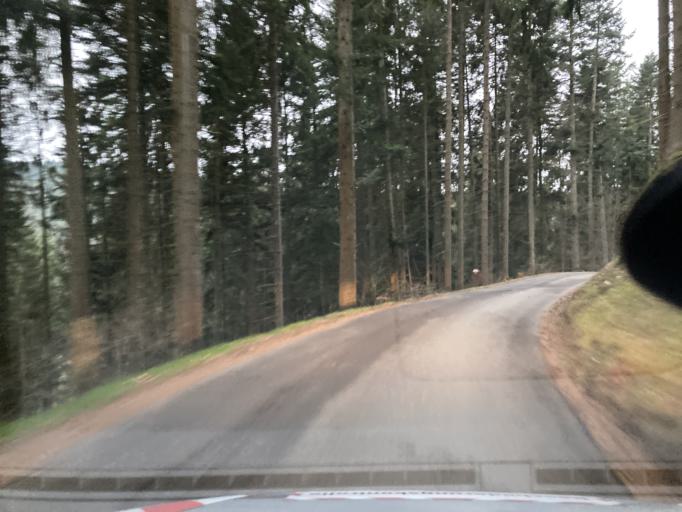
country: DE
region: Baden-Wuerttemberg
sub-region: Karlsruhe Region
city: Neubulach
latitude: 48.6677
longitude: 8.6541
